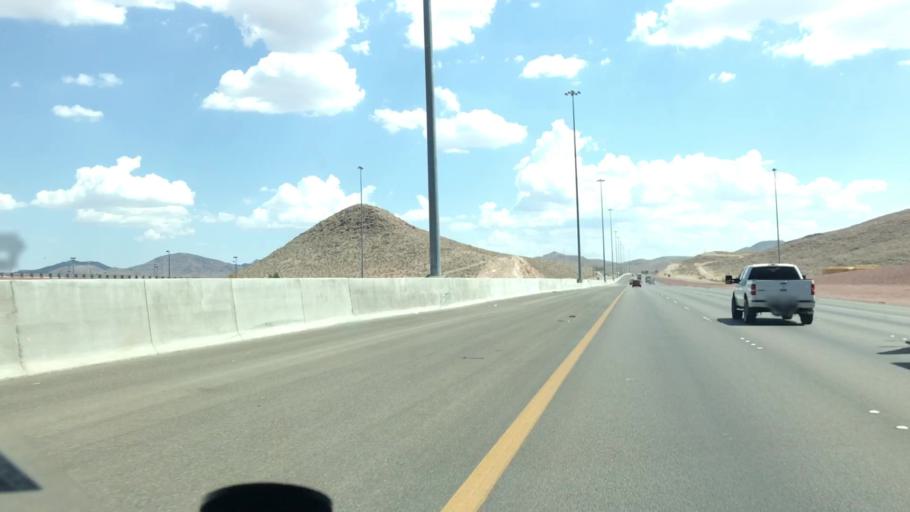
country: US
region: Nevada
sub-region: Clark County
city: Enterprise
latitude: 35.9605
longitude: -115.1814
